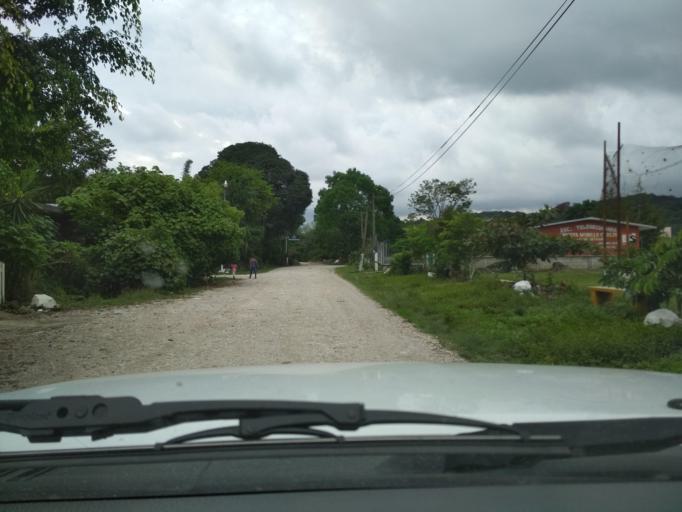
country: MX
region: Veracruz
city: Paraje Nuevo
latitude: 18.8782
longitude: -96.8819
